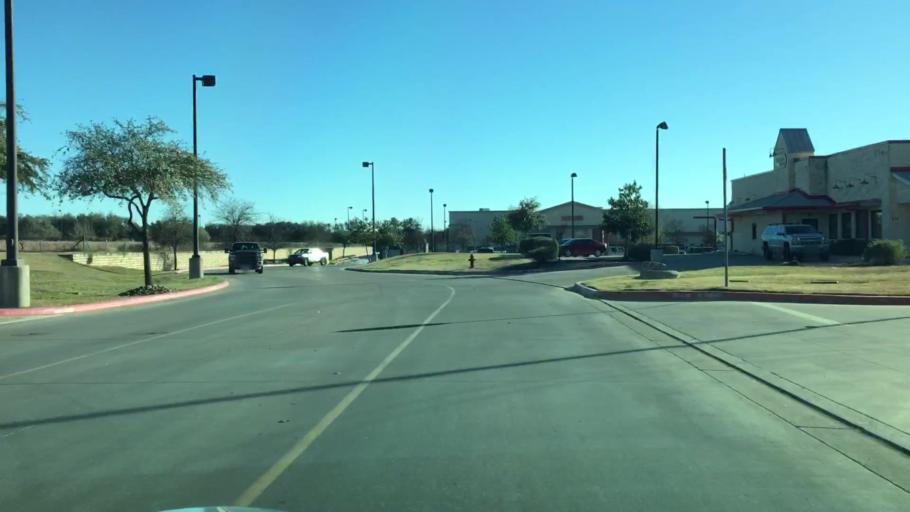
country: US
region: Texas
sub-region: Hays County
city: Dripping Springs
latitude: 30.1909
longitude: -98.0850
